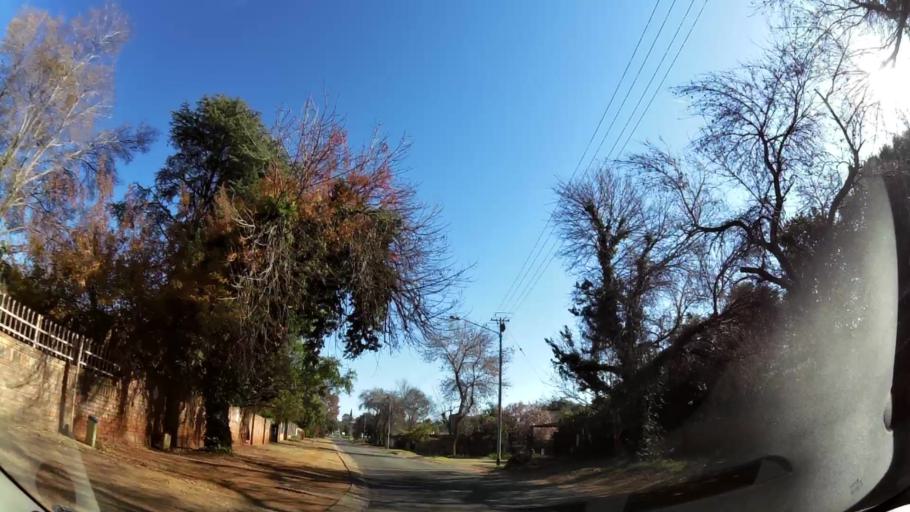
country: ZA
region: Gauteng
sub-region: City of Tshwane Metropolitan Municipality
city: Centurion
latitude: -25.8522
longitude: 28.2083
